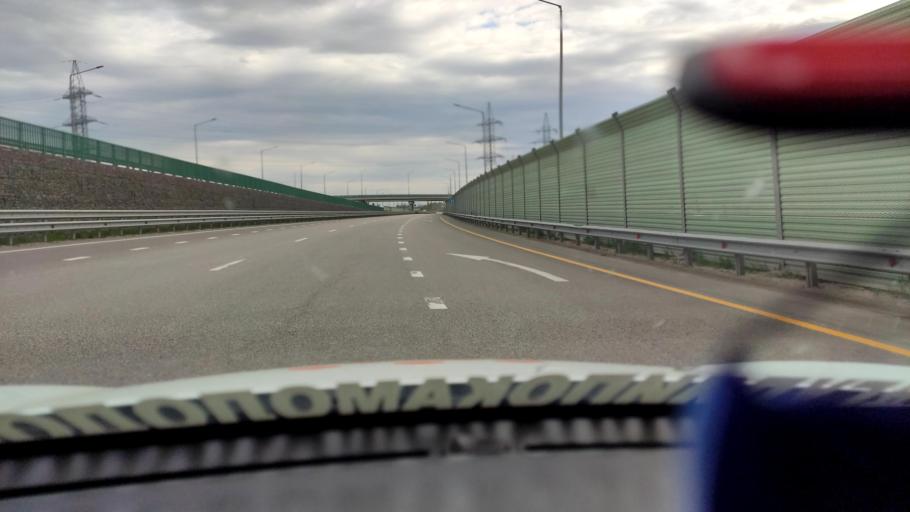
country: RU
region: Voronezj
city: Novaya Usman'
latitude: 51.6408
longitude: 39.3168
